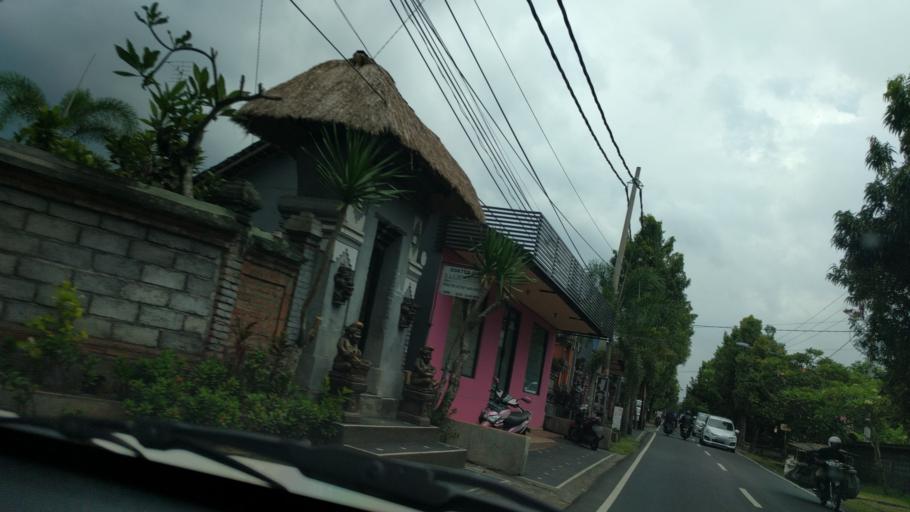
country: ID
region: Bali
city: Banjar Pande
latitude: -8.5130
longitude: 115.2407
